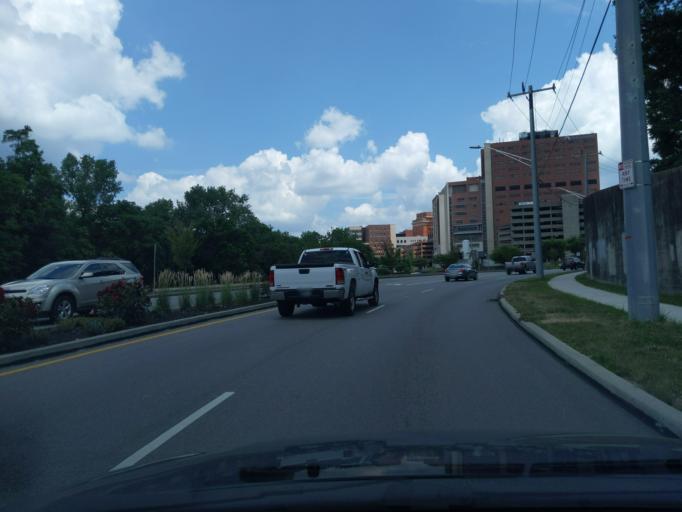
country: US
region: Ohio
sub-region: Hamilton County
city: Saint Bernard
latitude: 39.1401
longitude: -84.5262
